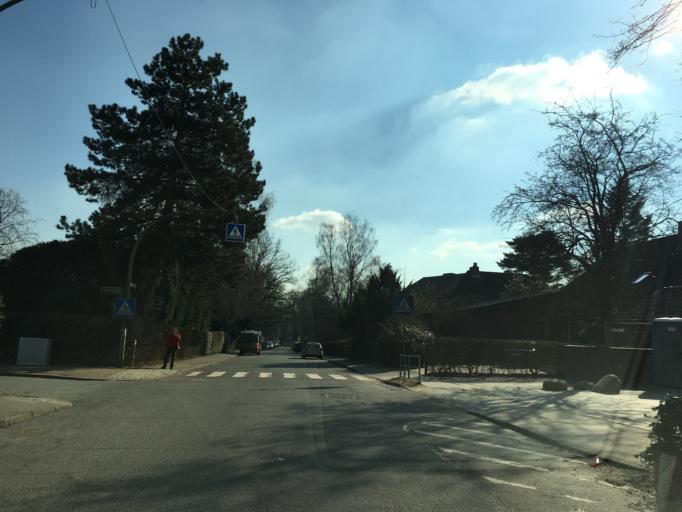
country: DE
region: Hamburg
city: Eidelstedt
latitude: 53.5671
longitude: 9.8719
